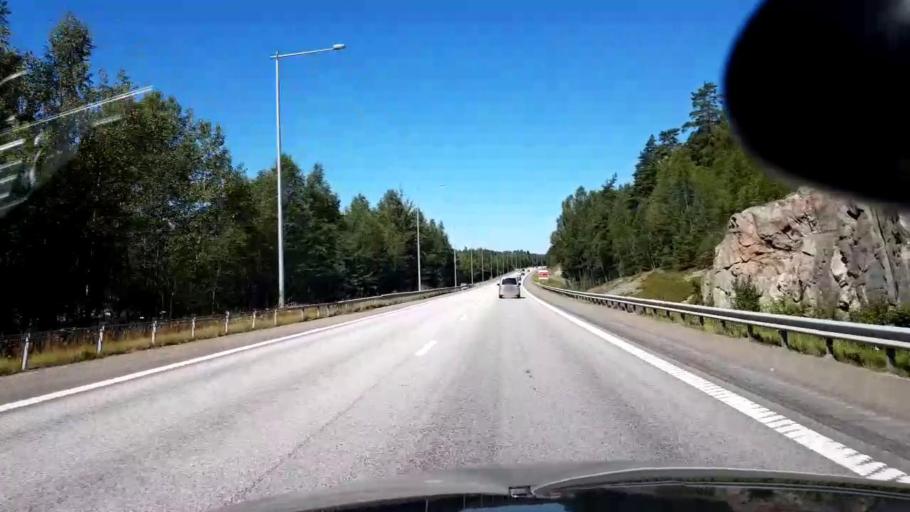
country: SE
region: Stockholm
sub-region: Upplands-Bro Kommun
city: Bro
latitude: 59.5127
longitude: 17.6843
